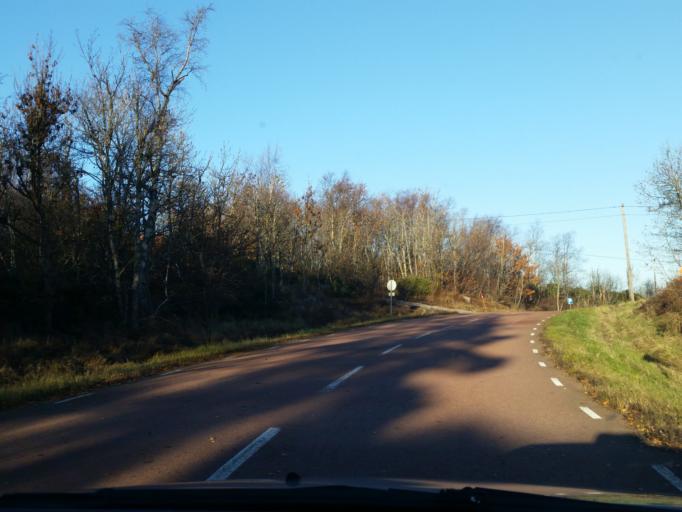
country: AX
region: Alands skaergard
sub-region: Braendoe
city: Braendoe
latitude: 60.3627
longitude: 21.0683
